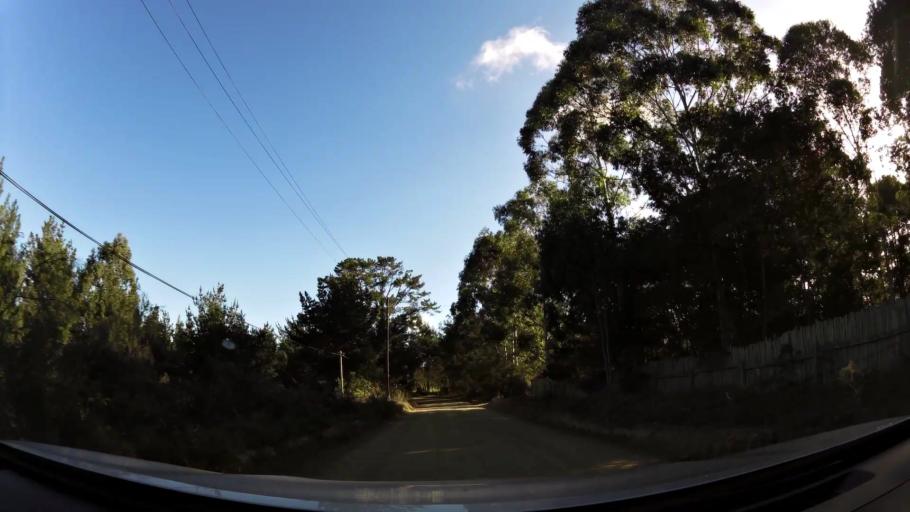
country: ZA
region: Western Cape
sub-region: Eden District Municipality
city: George
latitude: -33.9809
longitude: 22.5700
